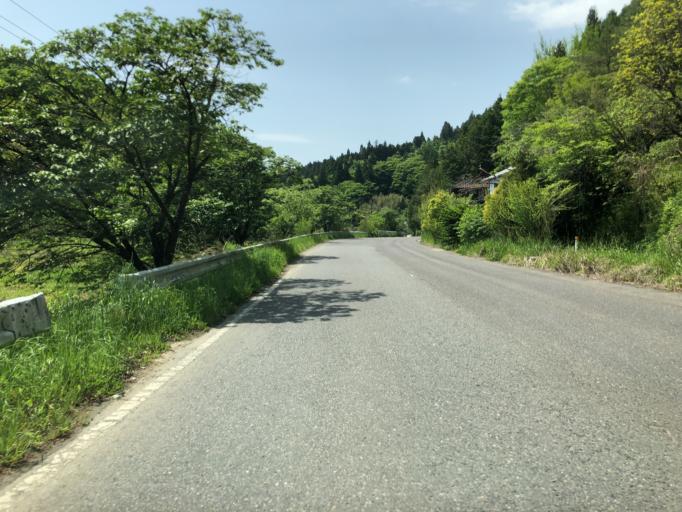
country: JP
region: Fukushima
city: Ishikawa
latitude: 37.1509
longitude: 140.5037
